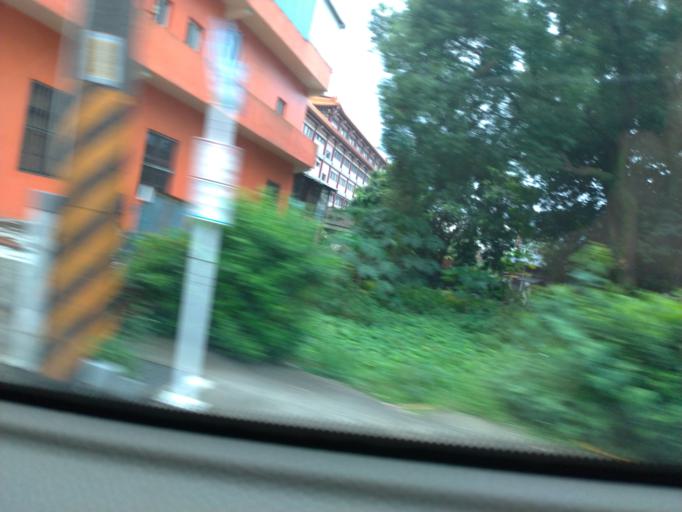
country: TW
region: Taipei
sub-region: Taipei
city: Banqiao
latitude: 24.9314
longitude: 121.4088
